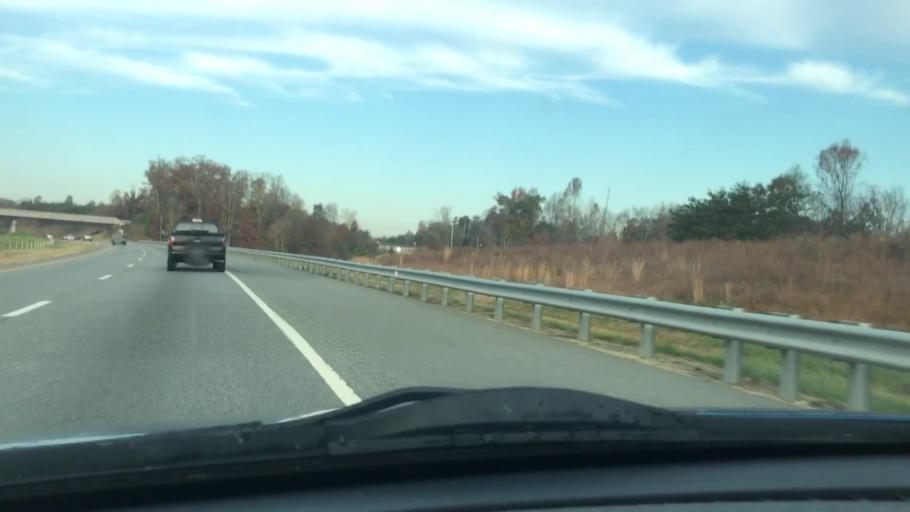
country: US
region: North Carolina
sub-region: Randolph County
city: Archdale
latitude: 35.9358
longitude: -79.9332
